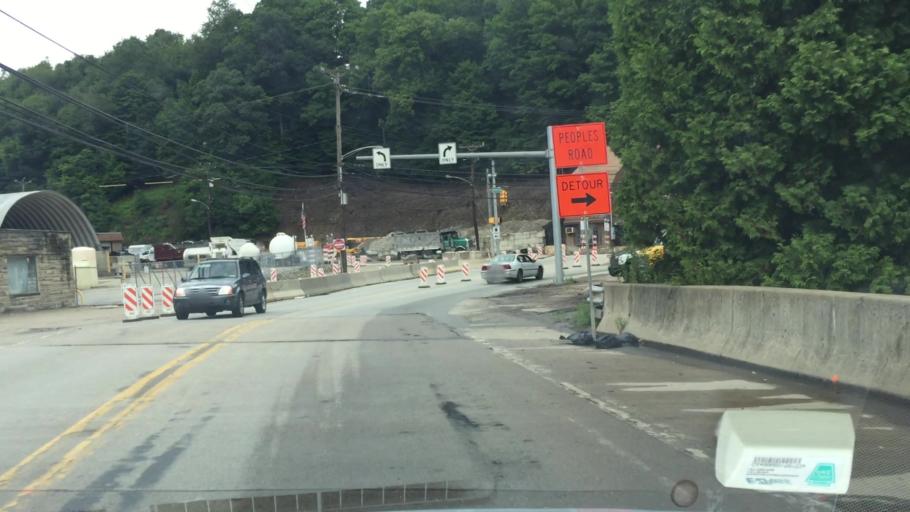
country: US
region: Pennsylvania
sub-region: Allegheny County
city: Millvale
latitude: 40.5055
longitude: -79.9900
